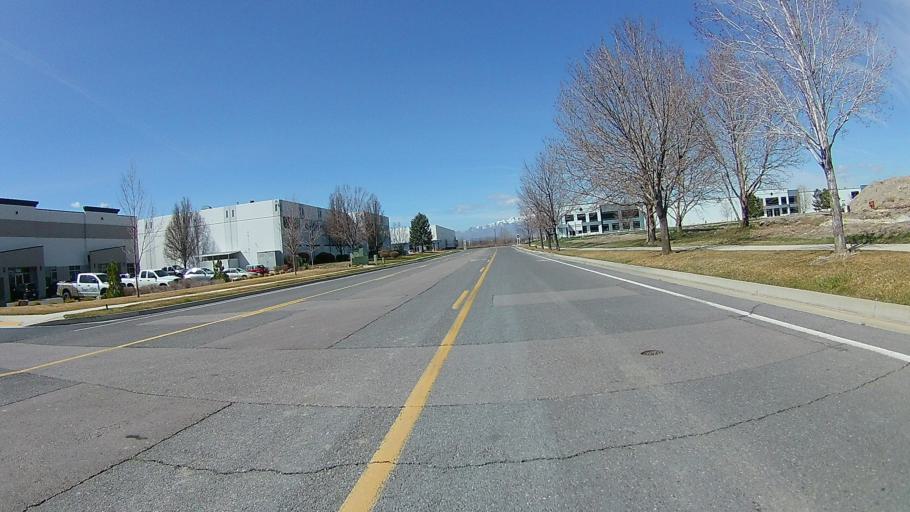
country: US
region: Utah
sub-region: Utah County
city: American Fork
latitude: 40.3514
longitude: -111.7790
